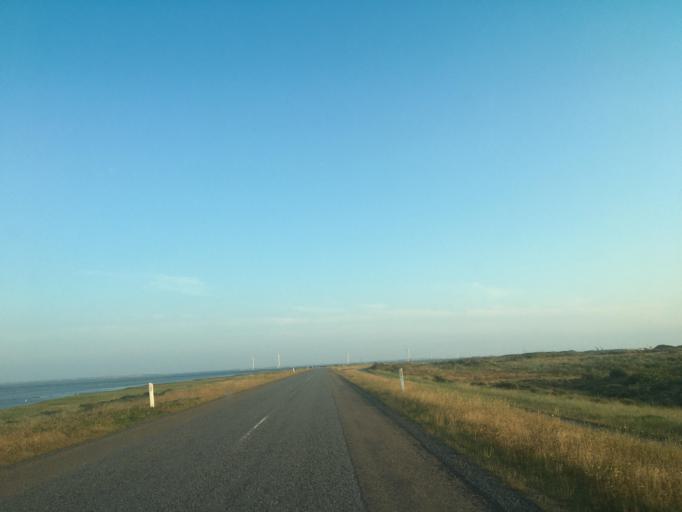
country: DK
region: Central Jutland
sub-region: Lemvig Kommune
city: Thyboron
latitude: 56.7167
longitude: 8.2488
